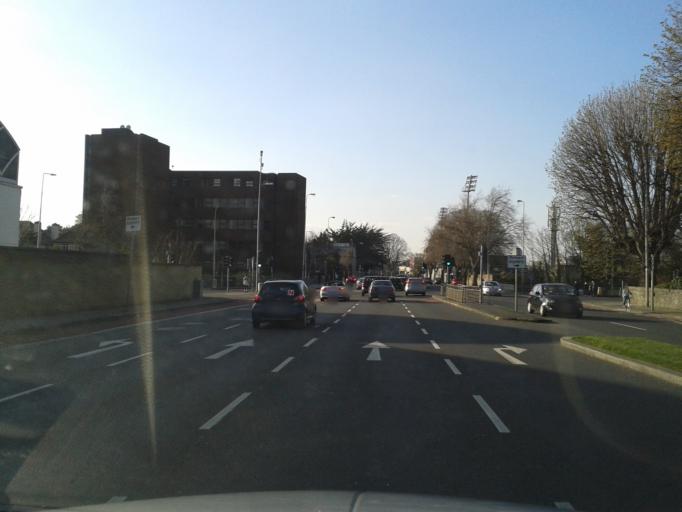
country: IE
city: Clonskeagh
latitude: 53.3186
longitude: -6.2314
